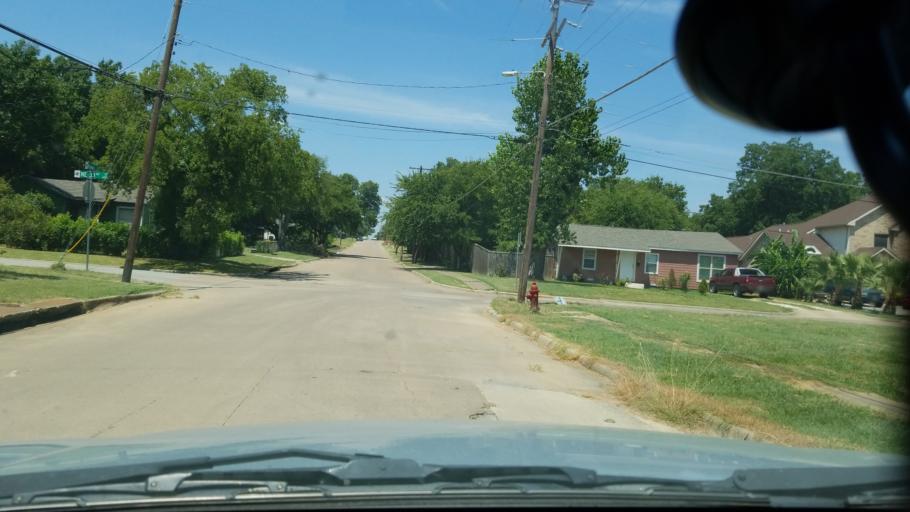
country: US
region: Texas
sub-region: Dallas County
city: Grand Prairie
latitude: 32.7562
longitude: -96.9552
